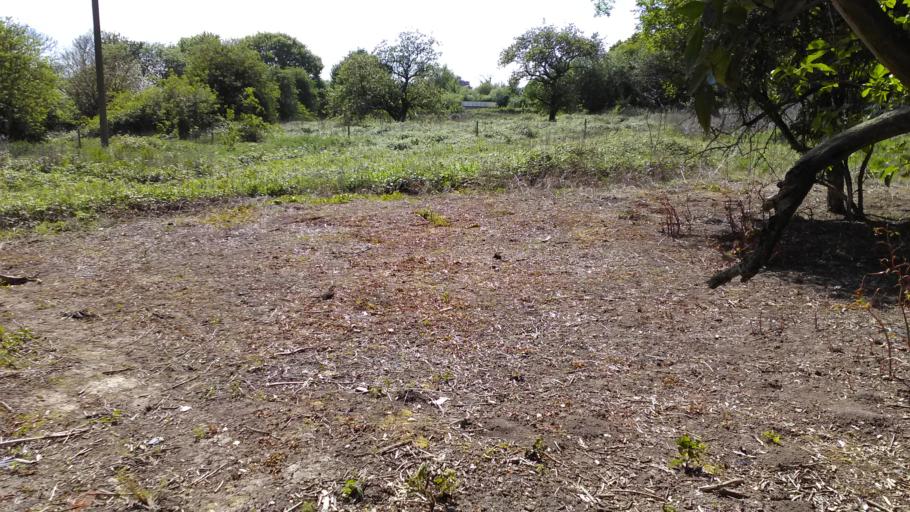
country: GB
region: England
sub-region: Nottinghamshire
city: Arnold
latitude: 52.9928
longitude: -1.1059
